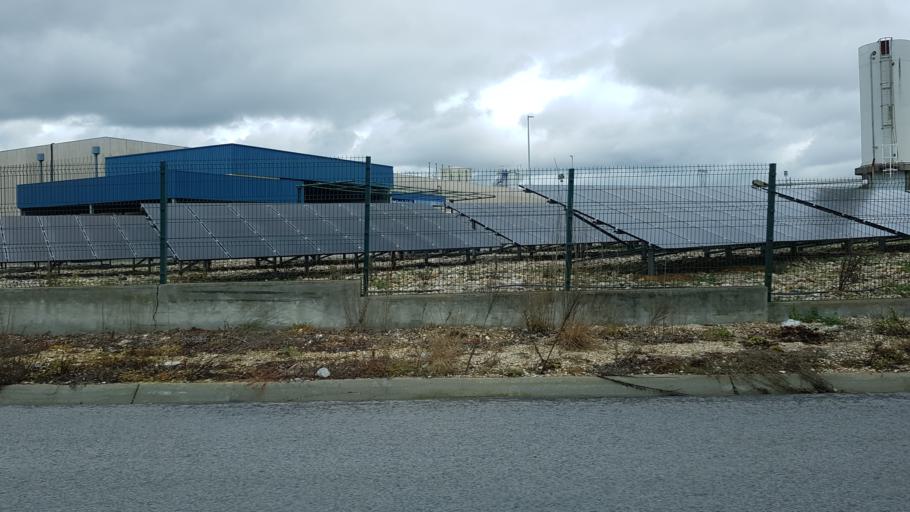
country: PT
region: Lisbon
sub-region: Alenquer
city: Carregado
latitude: 39.0320
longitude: -8.9747
